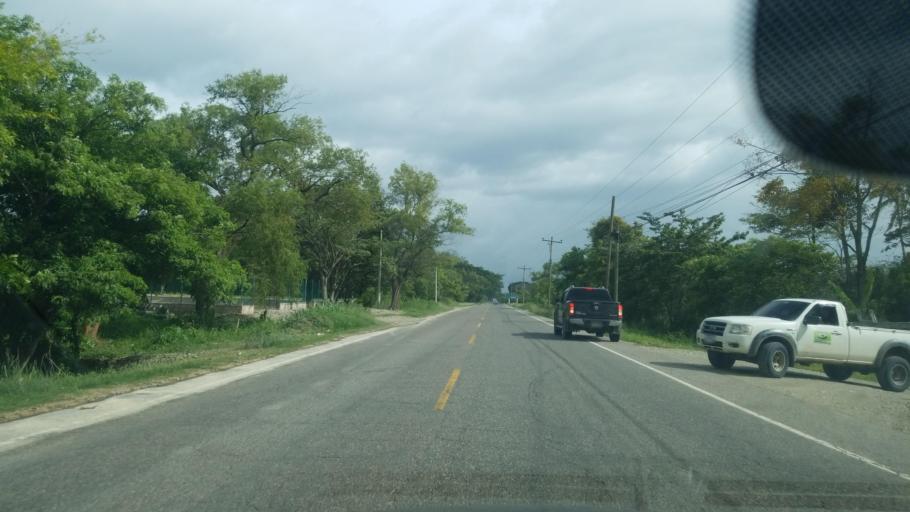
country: HN
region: Ocotepeque
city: Santa Lucia
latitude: 14.4110
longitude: -89.1949
